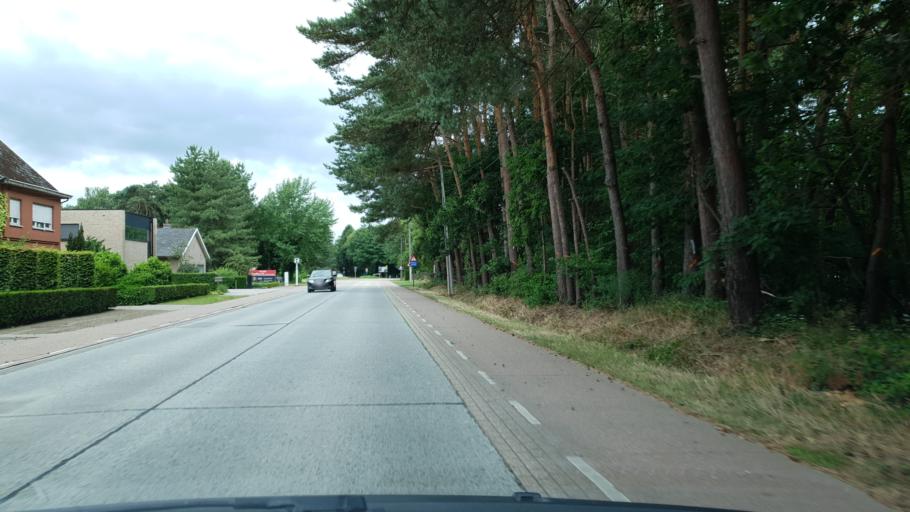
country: BE
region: Flanders
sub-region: Provincie Antwerpen
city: Westerlo
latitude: 51.0857
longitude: 4.8864
